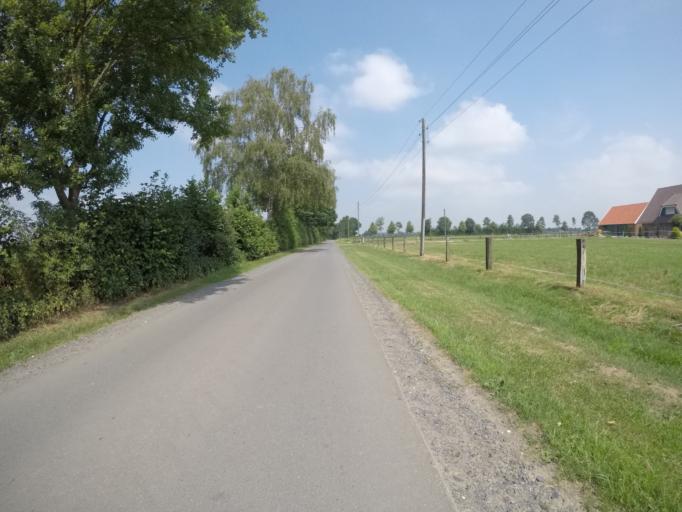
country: DE
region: North Rhine-Westphalia
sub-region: Regierungsbezirk Munster
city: Isselburg
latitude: 51.8364
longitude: 6.5271
